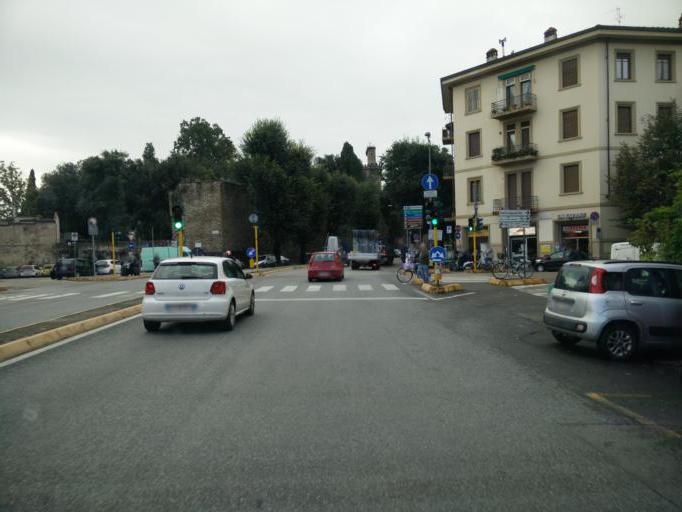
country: IT
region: Tuscany
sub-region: Province of Florence
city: Florence
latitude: 43.7671
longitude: 11.2401
